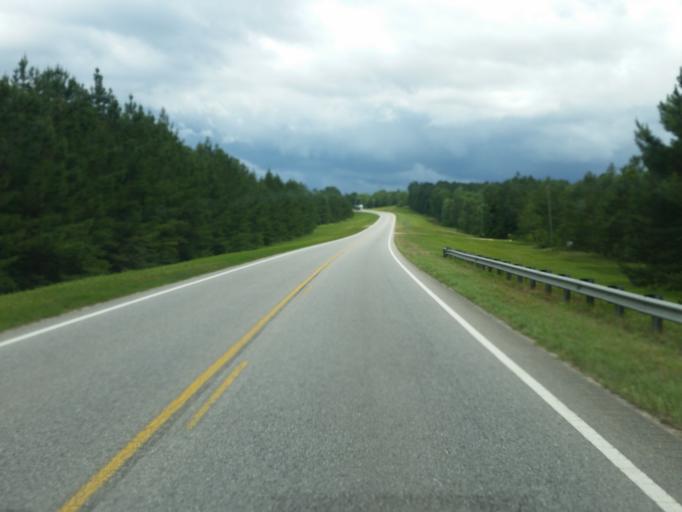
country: US
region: Mississippi
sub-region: George County
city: Lucedale
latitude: 30.8567
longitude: -88.4091
